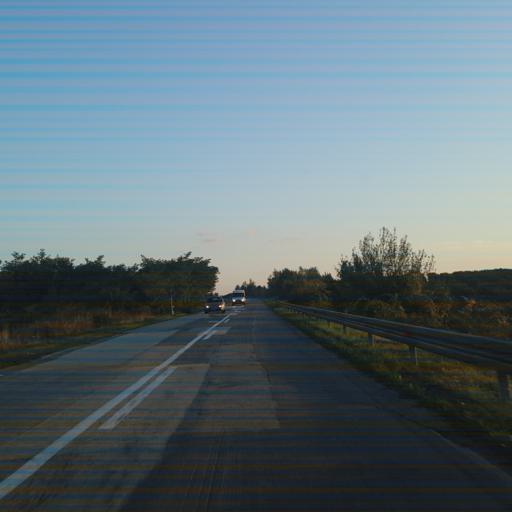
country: RS
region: Central Serbia
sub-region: Zajecarski Okrug
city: Zajecar
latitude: 44.0032
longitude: 22.3020
